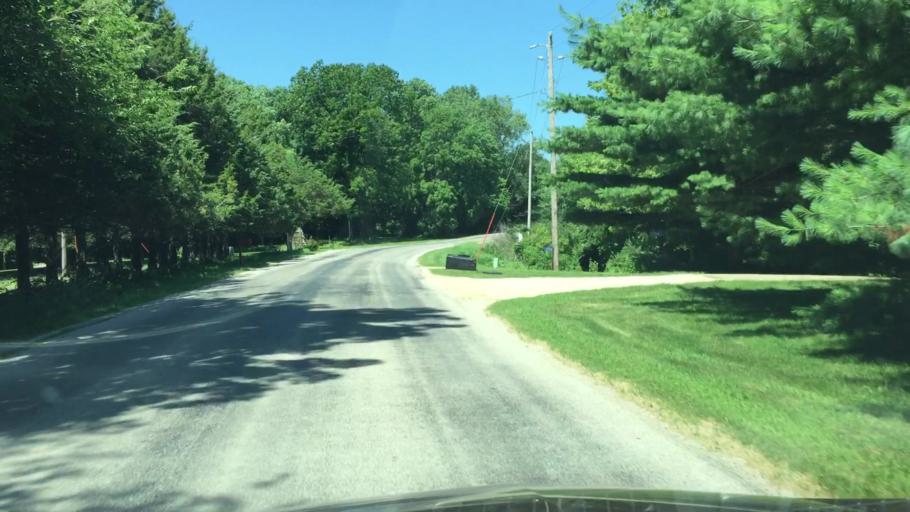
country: US
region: Iowa
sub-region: Linn County
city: Ely
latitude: 41.8149
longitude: -91.6012
